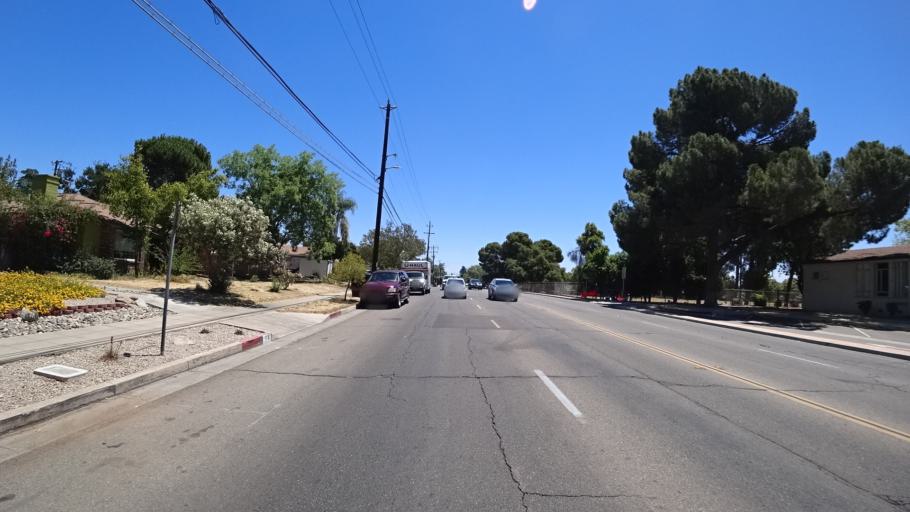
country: US
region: California
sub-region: Fresno County
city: Fresno
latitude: 36.7721
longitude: -119.8105
